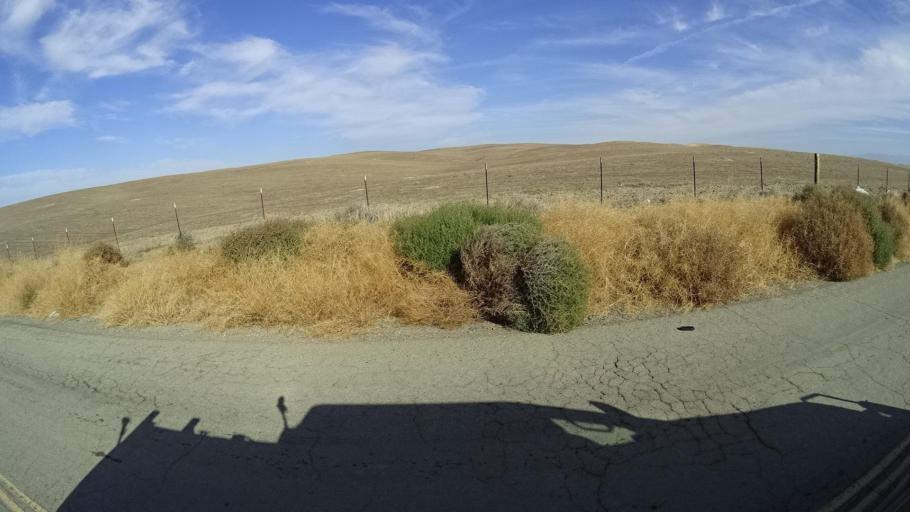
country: US
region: California
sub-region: Tulare County
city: Richgrove
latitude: 35.6221
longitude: -119.0119
